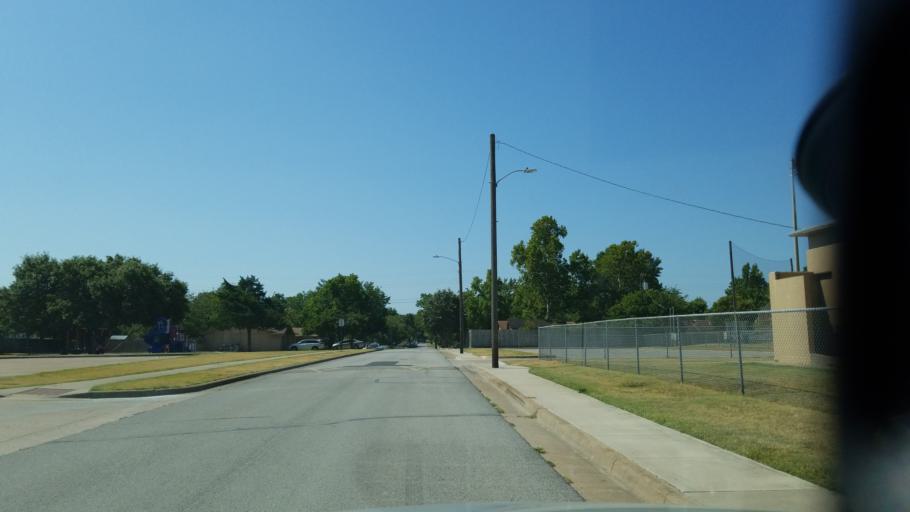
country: US
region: Texas
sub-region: Dallas County
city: Duncanville
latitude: 32.6441
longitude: -96.8990
